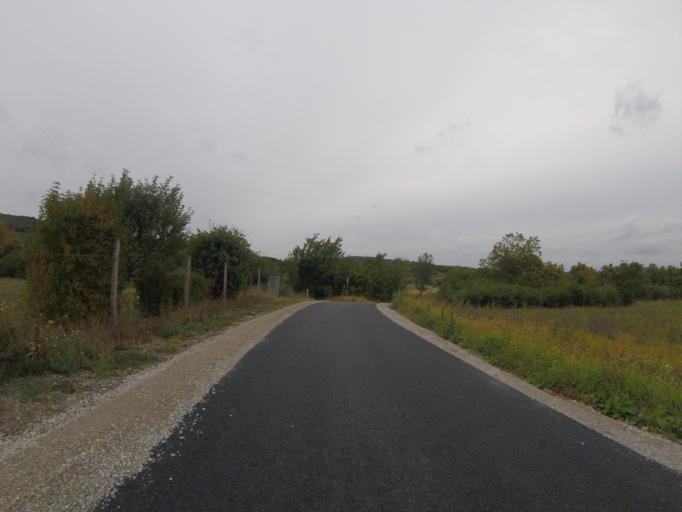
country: AT
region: Burgenland
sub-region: Politischer Bezirk Neusiedl am See
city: Winden am See
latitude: 47.9595
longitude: 16.7409
